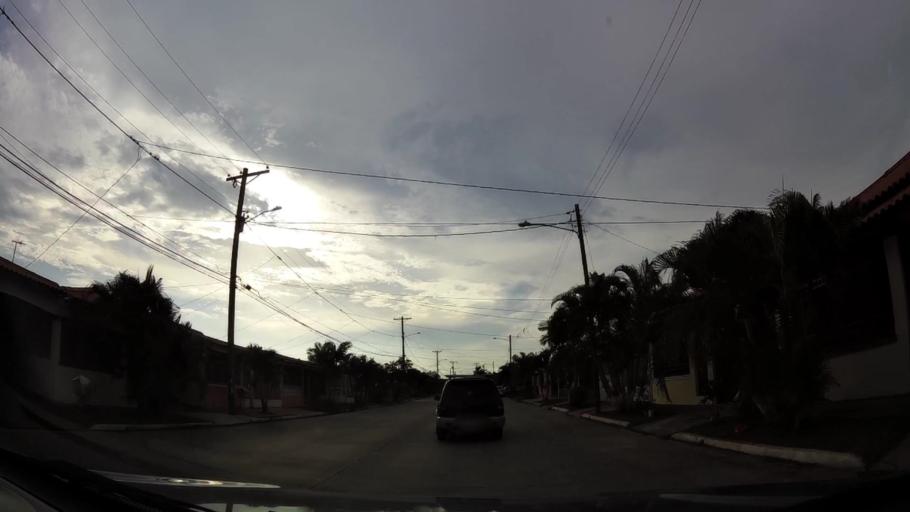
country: PA
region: Panama
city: Tocumen
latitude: 9.0738
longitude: -79.3619
